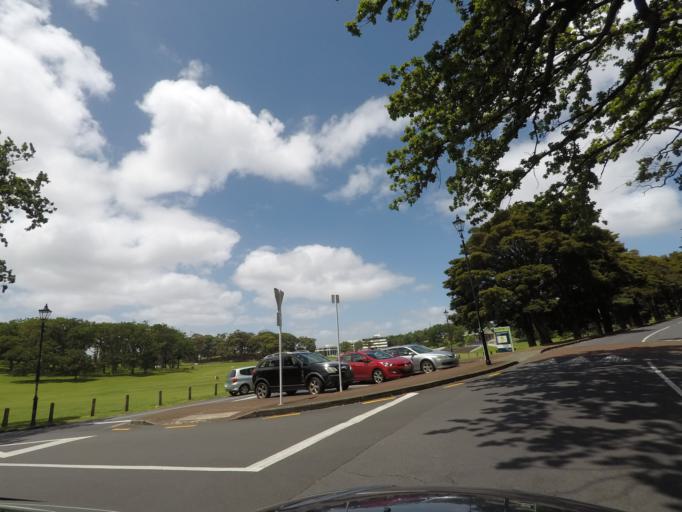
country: NZ
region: Auckland
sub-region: Auckland
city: Auckland
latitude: -36.8608
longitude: 174.7718
